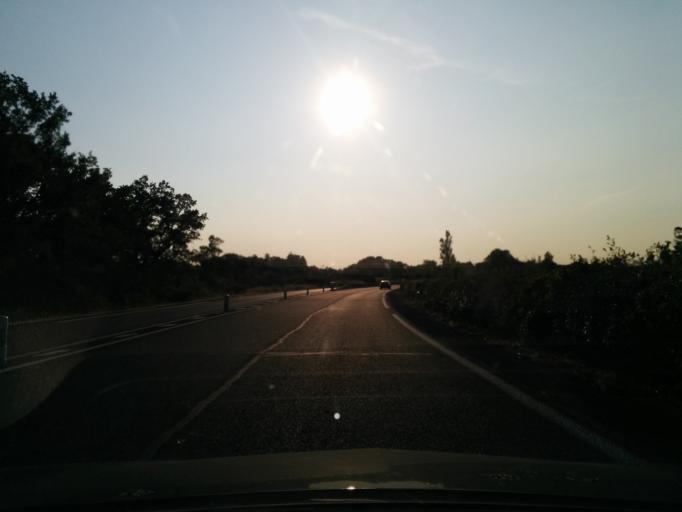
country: FR
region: Midi-Pyrenees
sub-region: Departement du Lot
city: Pradines
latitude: 44.5828
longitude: 1.4887
